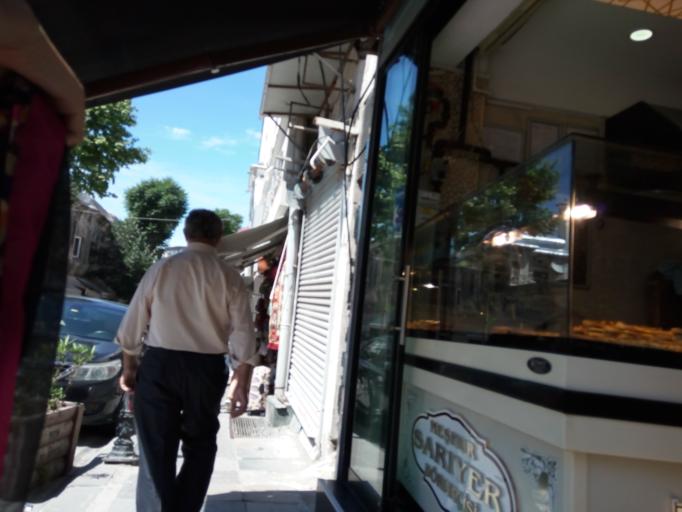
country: TR
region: Istanbul
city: Eminoenue
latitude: 41.0093
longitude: 28.9708
